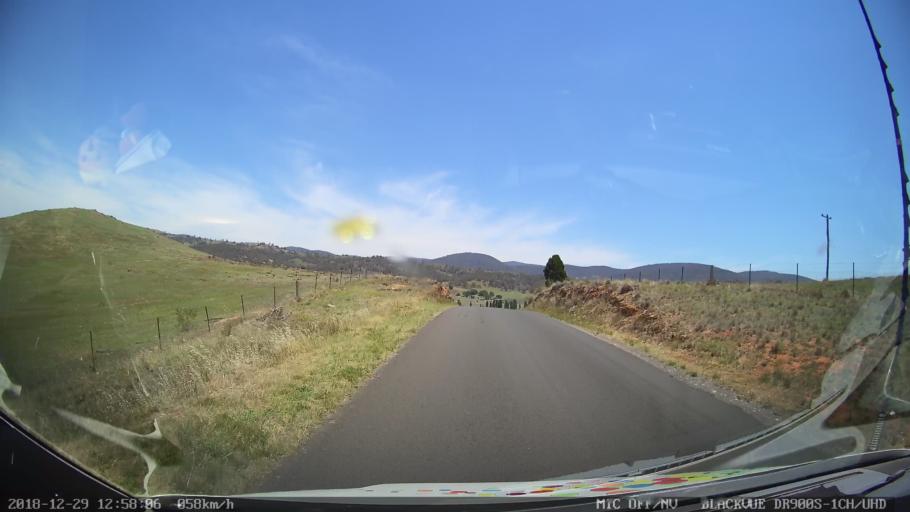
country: AU
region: Australian Capital Territory
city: Macarthur
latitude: -35.7100
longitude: 149.1706
